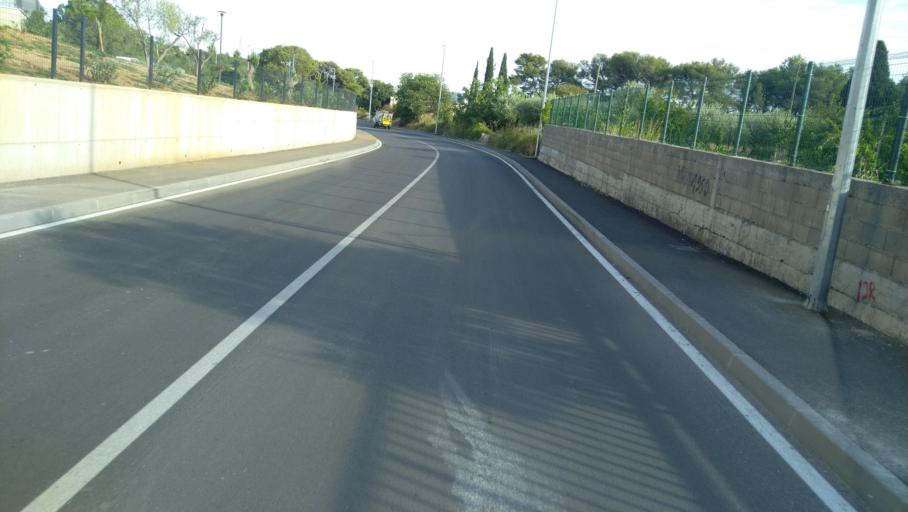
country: HR
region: Sibensko-Kniniska
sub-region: Grad Sibenik
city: Sibenik
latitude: 43.7193
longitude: 15.9122
